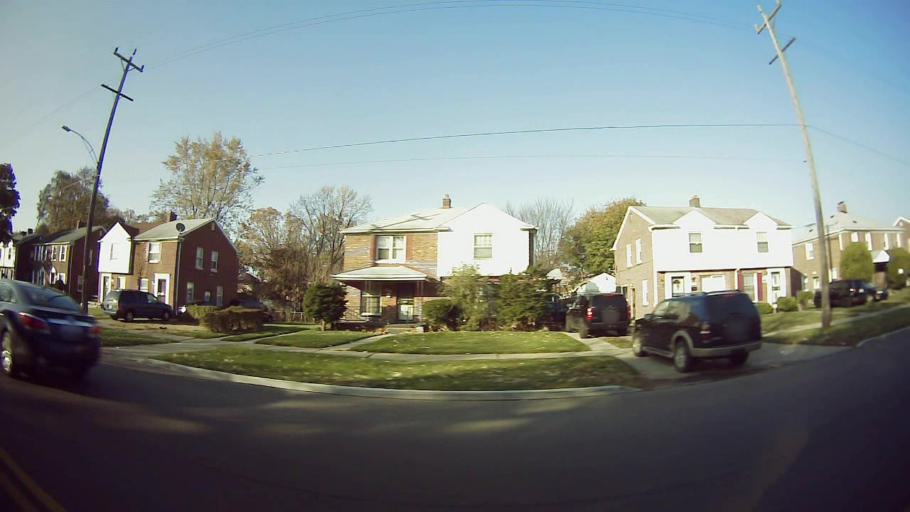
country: US
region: Michigan
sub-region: Oakland County
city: Oak Park
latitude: 42.4268
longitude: -83.1705
